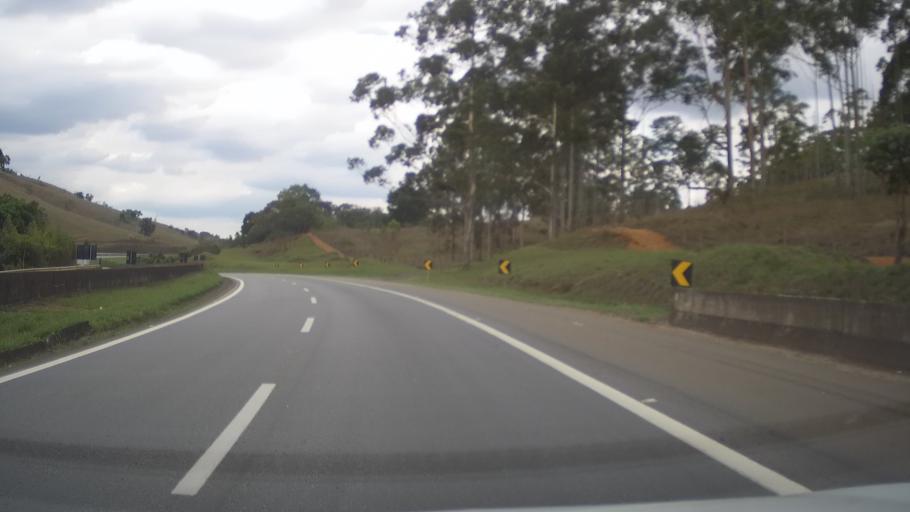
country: BR
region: Minas Gerais
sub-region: Tres Coracoes
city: Tres Coracoes
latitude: -21.5229
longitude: -45.2242
